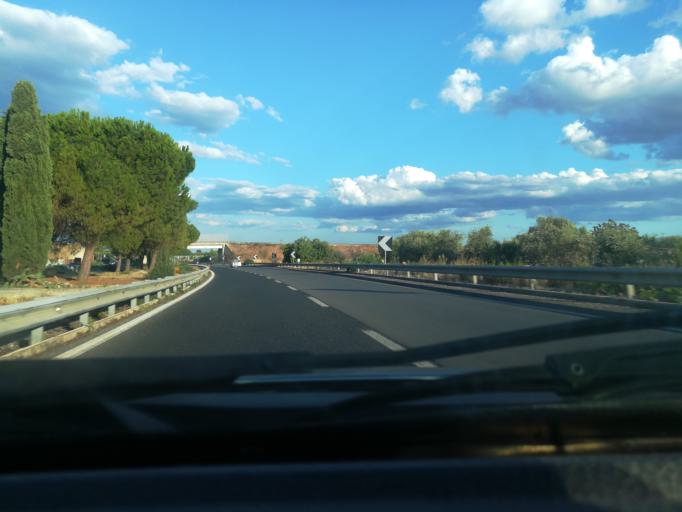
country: IT
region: Apulia
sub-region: Provincia di Bari
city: Mola di Bari
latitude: 41.0485
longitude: 17.0784
